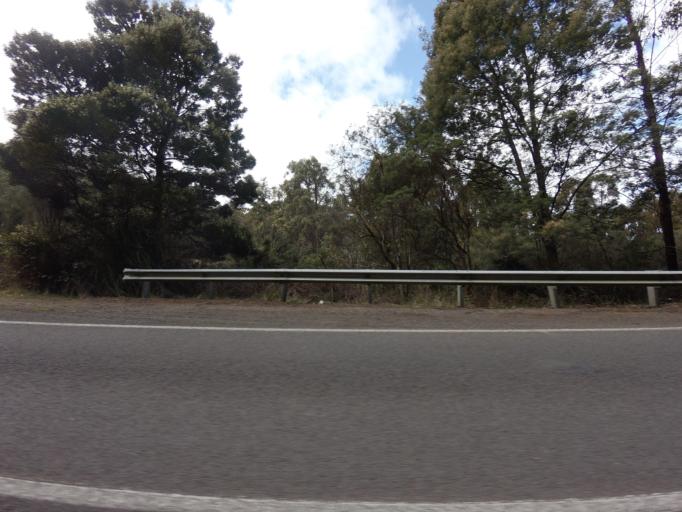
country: AU
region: Tasmania
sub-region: Huon Valley
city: Geeveston
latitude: -43.4087
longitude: 146.9588
